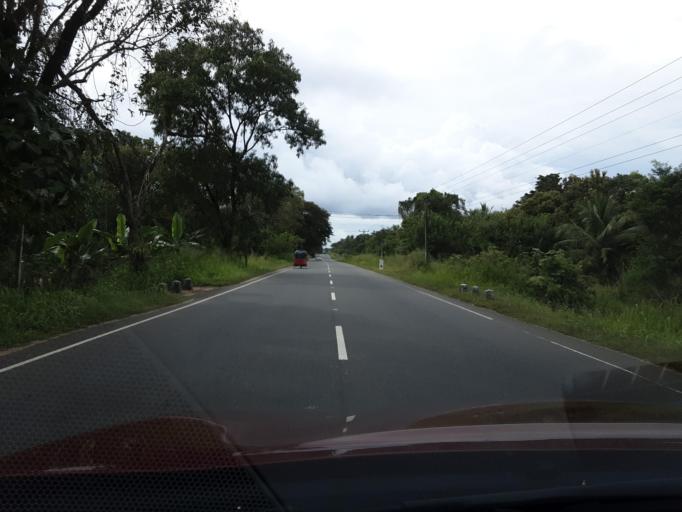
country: LK
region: Uva
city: Badulla
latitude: 7.3922
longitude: 81.1325
